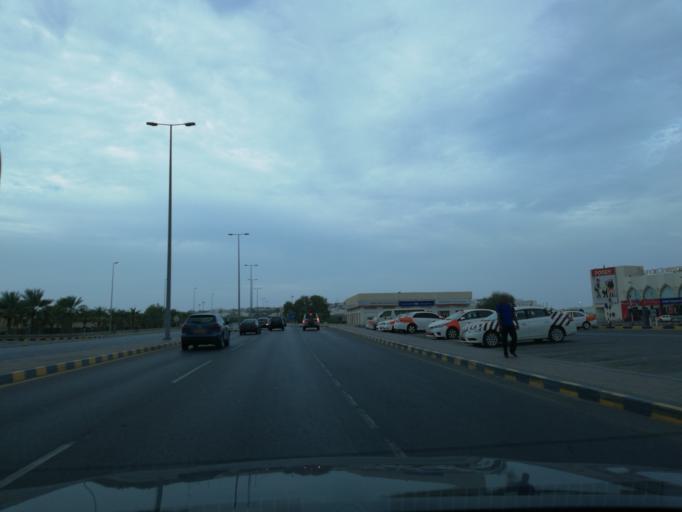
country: OM
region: Muhafazat Masqat
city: Muscat
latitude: 23.6124
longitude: 58.4931
